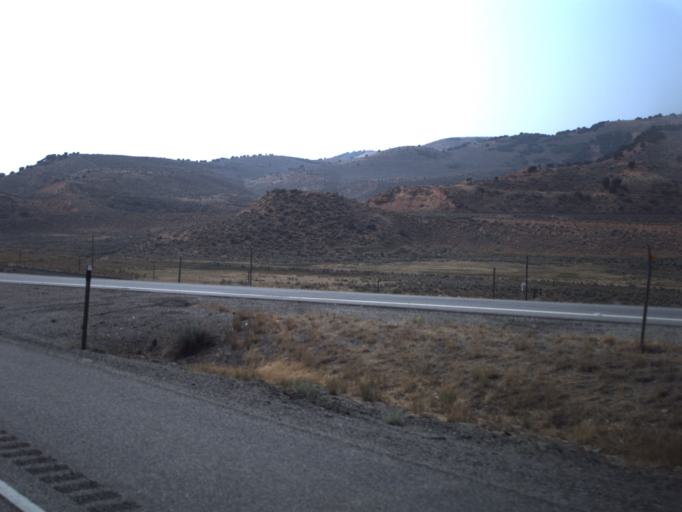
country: US
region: Wyoming
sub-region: Uinta County
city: Evanston
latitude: 41.1172
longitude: -111.1950
